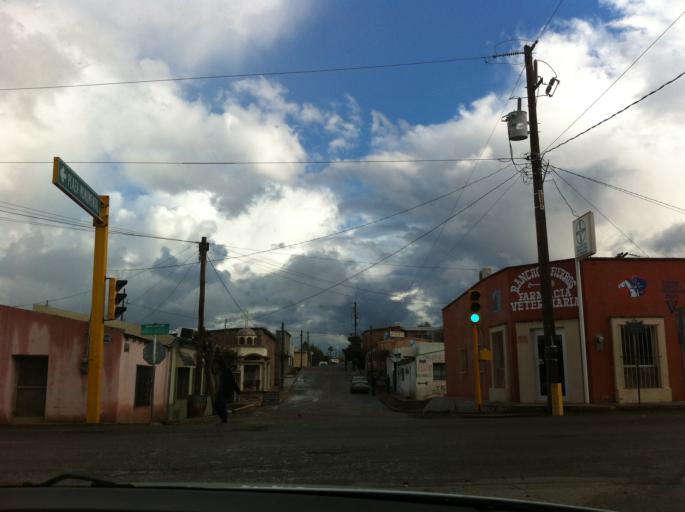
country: MX
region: Sonora
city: Magdalena de Kino
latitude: 30.6274
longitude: -110.9706
